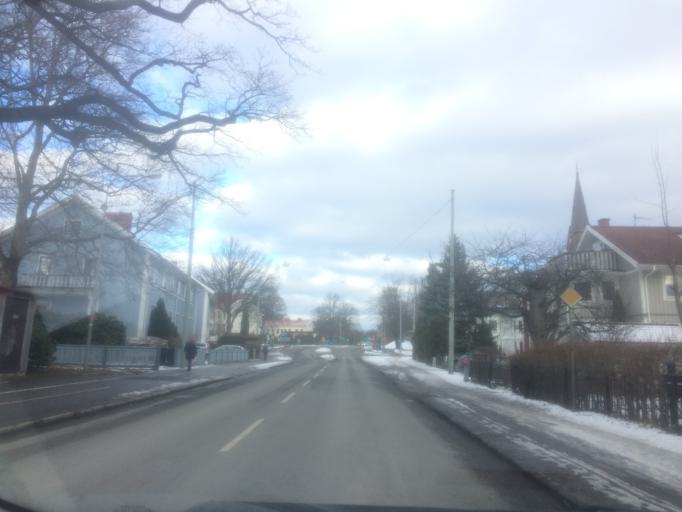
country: SE
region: Vaestra Goetaland
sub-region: Goteborg
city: Goeteborg
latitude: 57.7016
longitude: 12.0025
